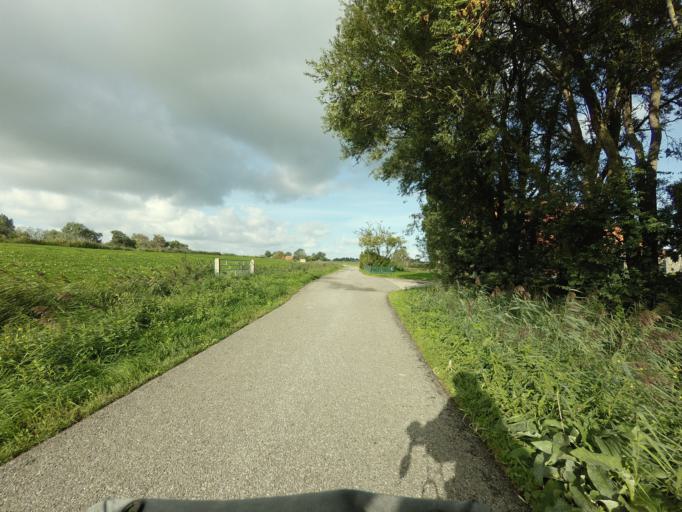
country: NL
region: Friesland
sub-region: Sudwest Fryslan
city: Makkum
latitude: 53.0559
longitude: 5.4313
